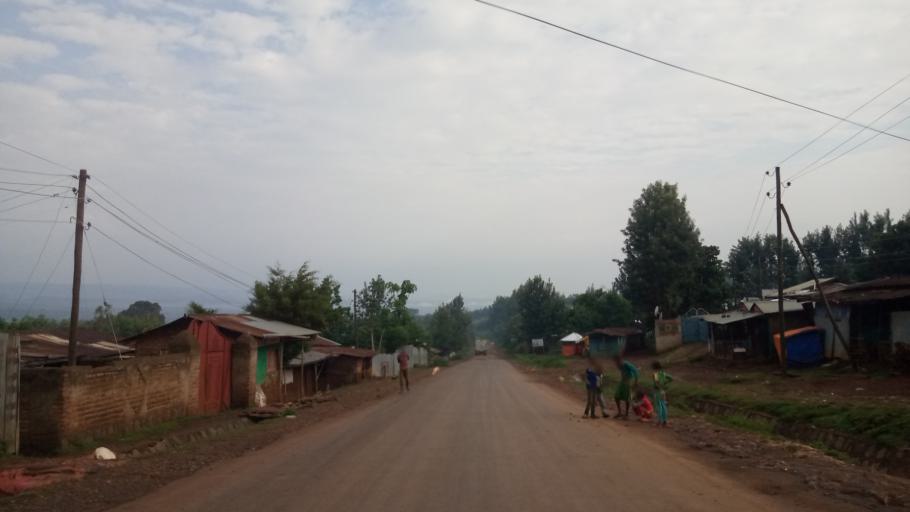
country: ET
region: Oromiya
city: Agaro
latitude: 7.7905
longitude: 36.7268
